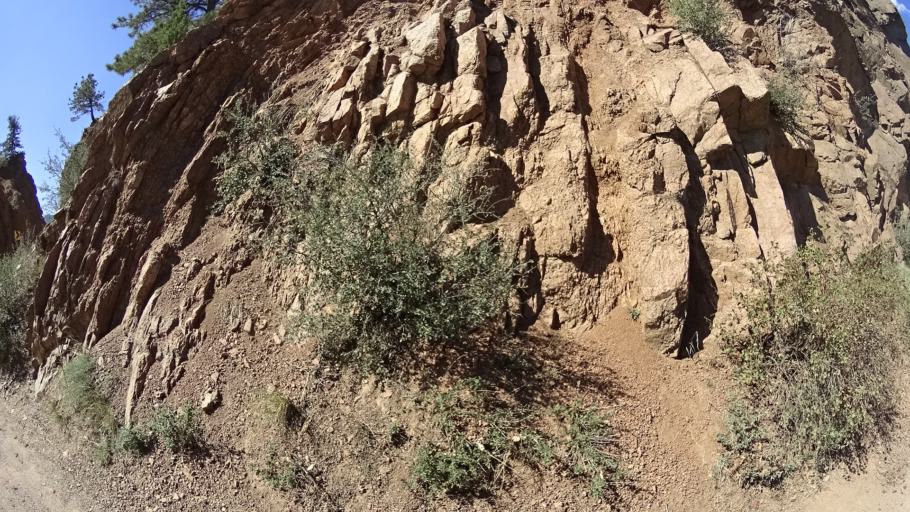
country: US
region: Colorado
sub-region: El Paso County
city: Colorado Springs
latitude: 38.7956
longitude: -104.8756
